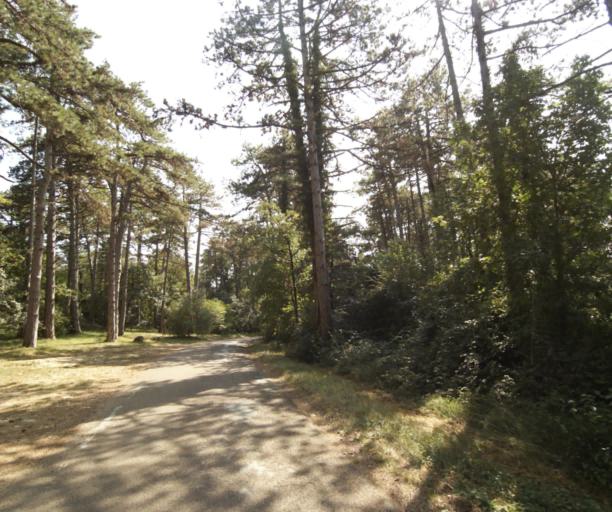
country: FR
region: Bourgogne
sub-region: Departement de Saone-et-Loire
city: Tournus
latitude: 46.5796
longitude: 4.8918
